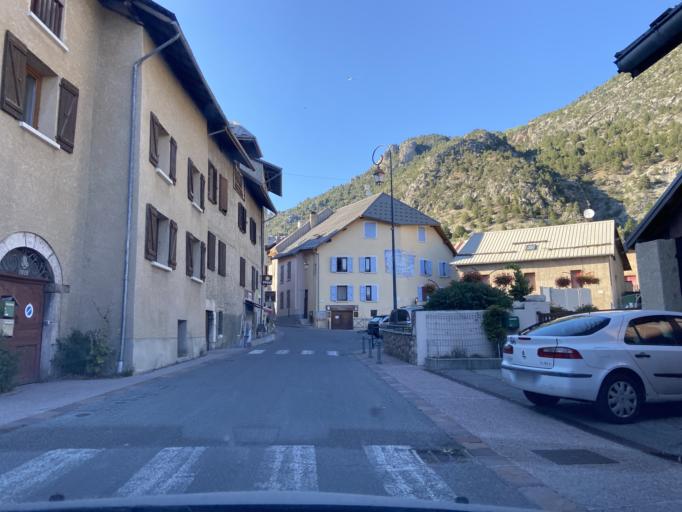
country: FR
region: Provence-Alpes-Cote d'Azur
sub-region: Departement des Hautes-Alpes
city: Guillestre
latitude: 44.7061
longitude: 6.6081
